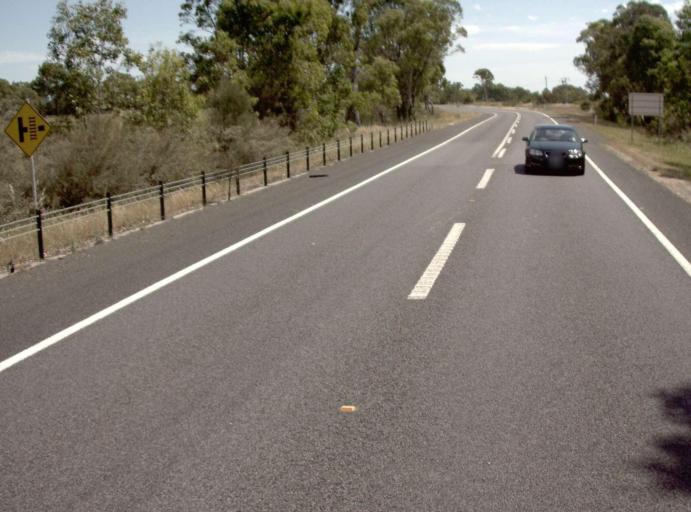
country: AU
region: Victoria
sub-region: Wellington
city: Sale
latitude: -37.9559
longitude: 147.1000
